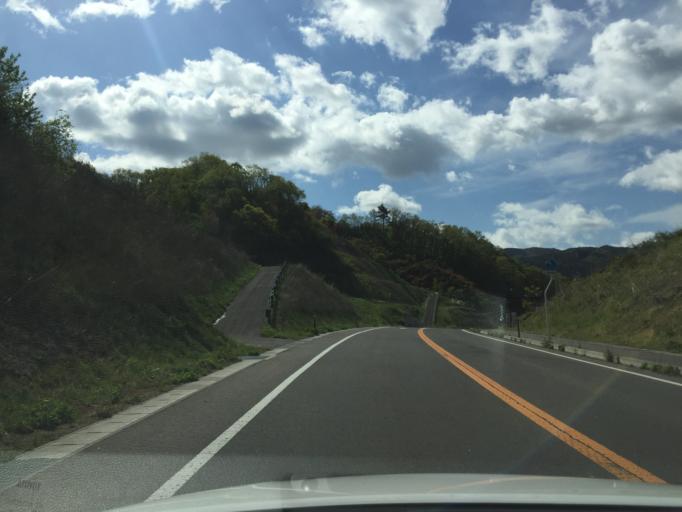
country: JP
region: Fukushima
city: Fukushima-shi
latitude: 37.6522
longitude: 140.6116
